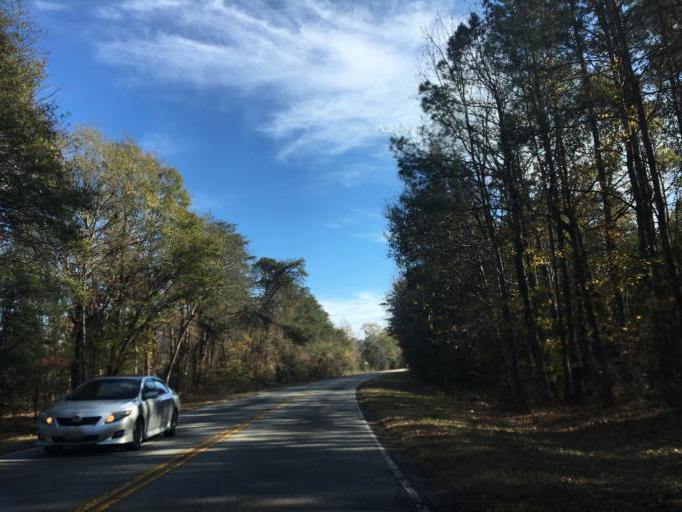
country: US
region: South Carolina
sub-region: Spartanburg County
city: Wellford
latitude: 34.9675
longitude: -82.0883
